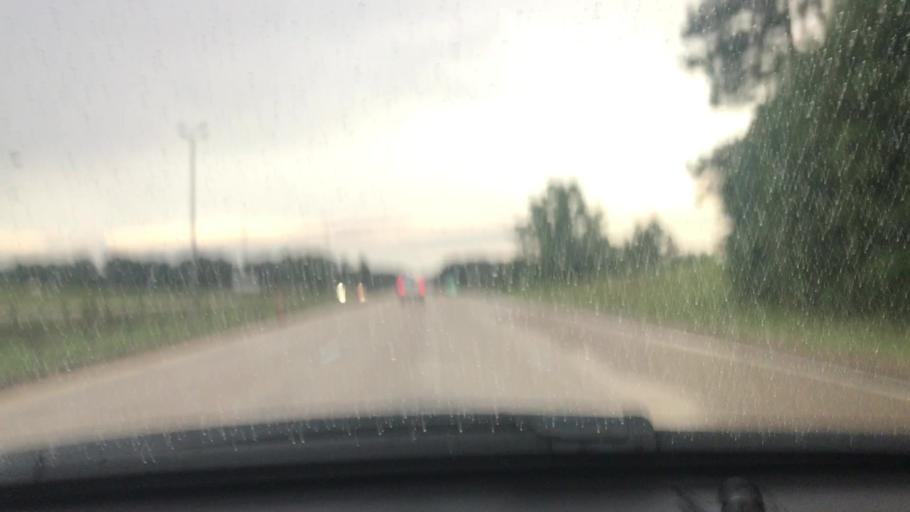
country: US
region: Mississippi
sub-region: Pike County
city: McComb
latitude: 31.2443
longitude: -90.4806
